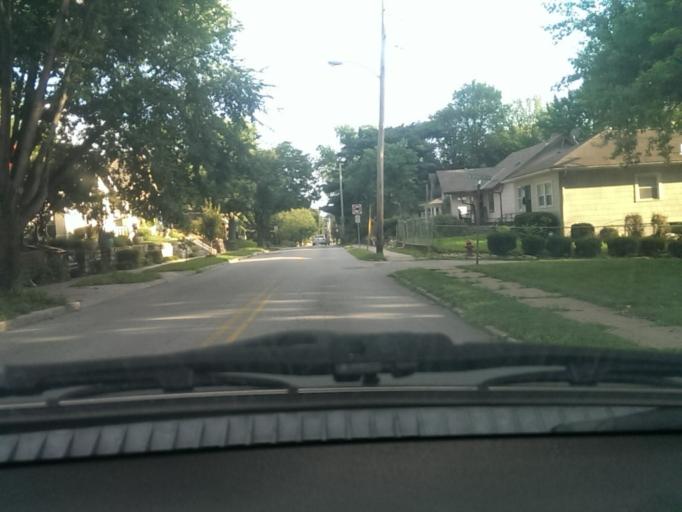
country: US
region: Kansas
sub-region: Johnson County
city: Westwood
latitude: 39.0492
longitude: -94.6074
